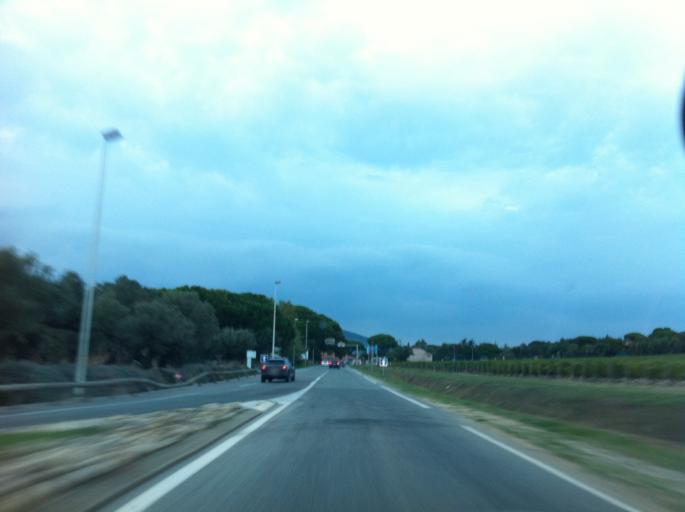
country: FR
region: Provence-Alpes-Cote d'Azur
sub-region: Departement du Var
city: Gassin
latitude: 43.2573
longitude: 6.5947
